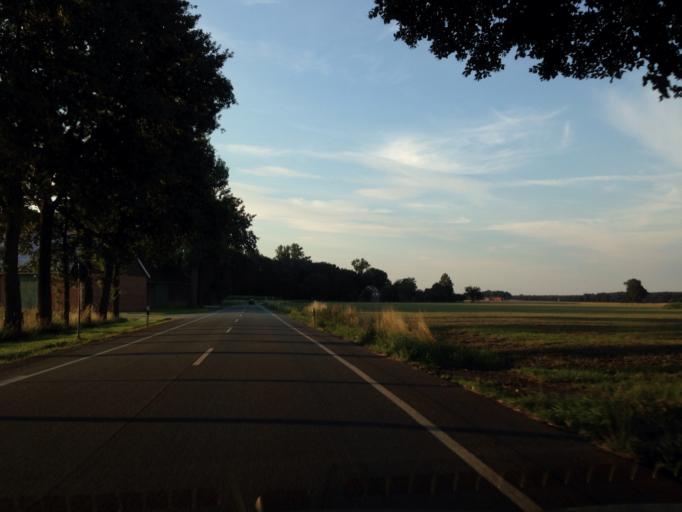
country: DE
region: North Rhine-Westphalia
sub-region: Regierungsbezirk Munster
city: Senden
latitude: 51.8545
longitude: 7.5471
